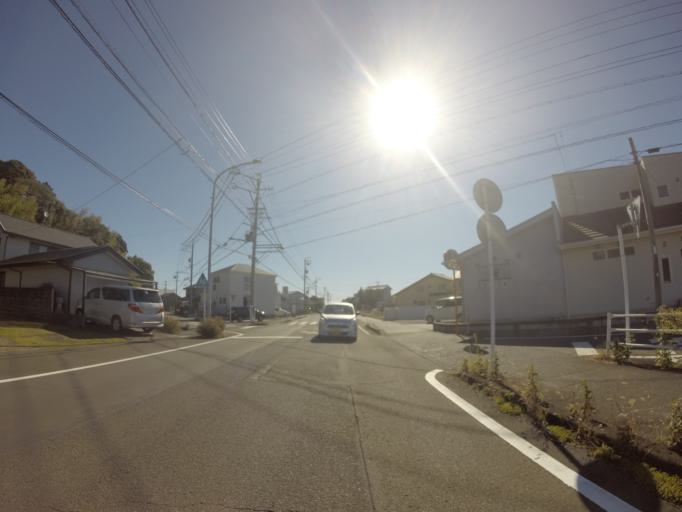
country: JP
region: Shizuoka
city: Fujieda
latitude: 34.8415
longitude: 138.2380
